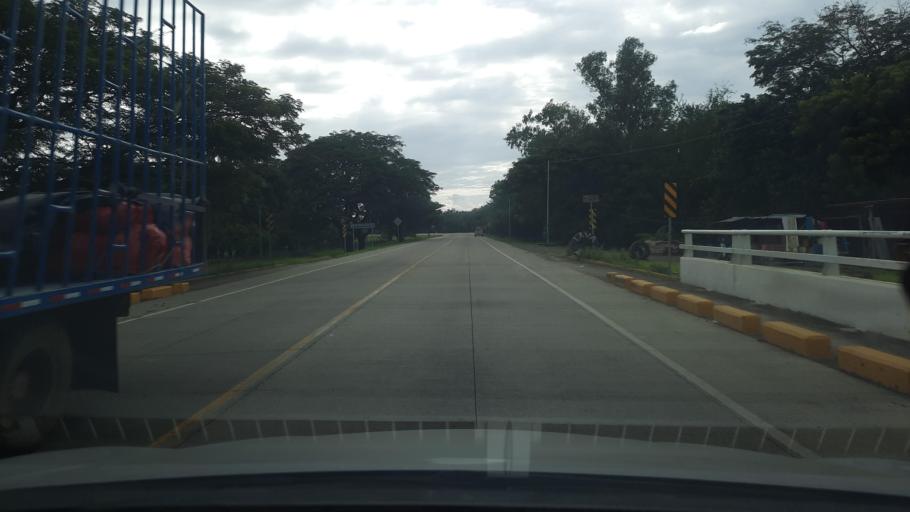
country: NI
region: Chinandega
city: Somotillo
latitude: 12.8605
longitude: -86.8612
